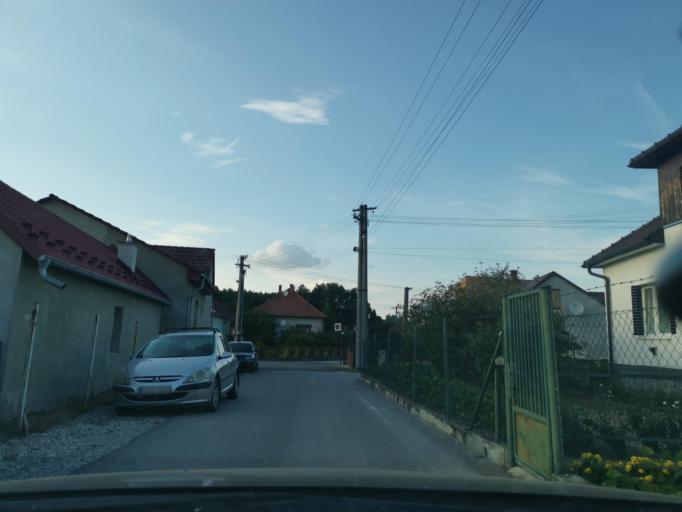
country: SK
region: Trnavsky
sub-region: Okres Senica
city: Senica
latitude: 48.6557
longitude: 17.2692
